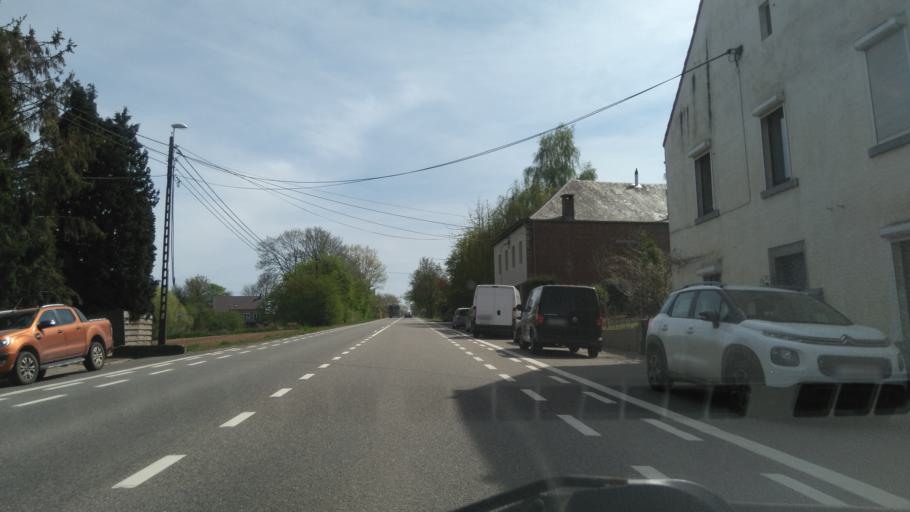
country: BE
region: Wallonia
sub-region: Province du Brabant Wallon
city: Ramillies
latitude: 50.6272
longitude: 4.8731
